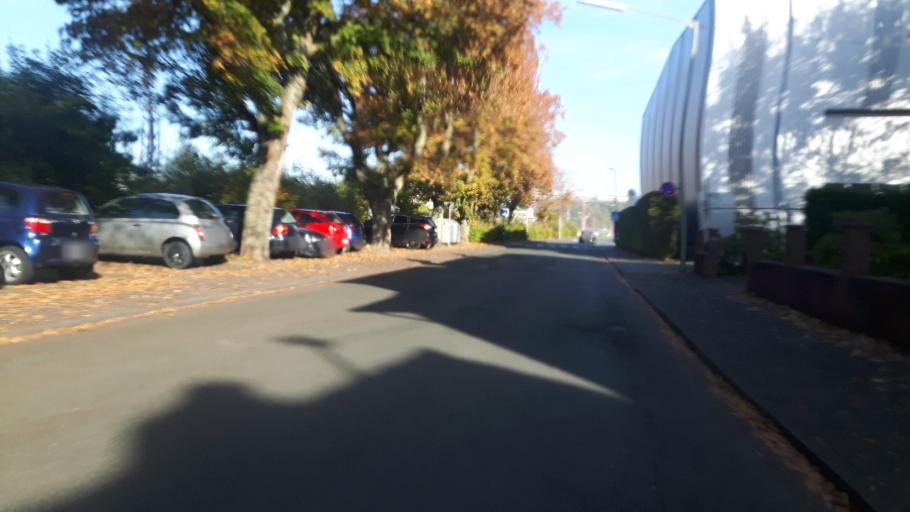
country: DE
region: North Rhine-Westphalia
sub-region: Regierungsbezirk Arnsberg
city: Siegen
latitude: 50.8910
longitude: 8.0307
